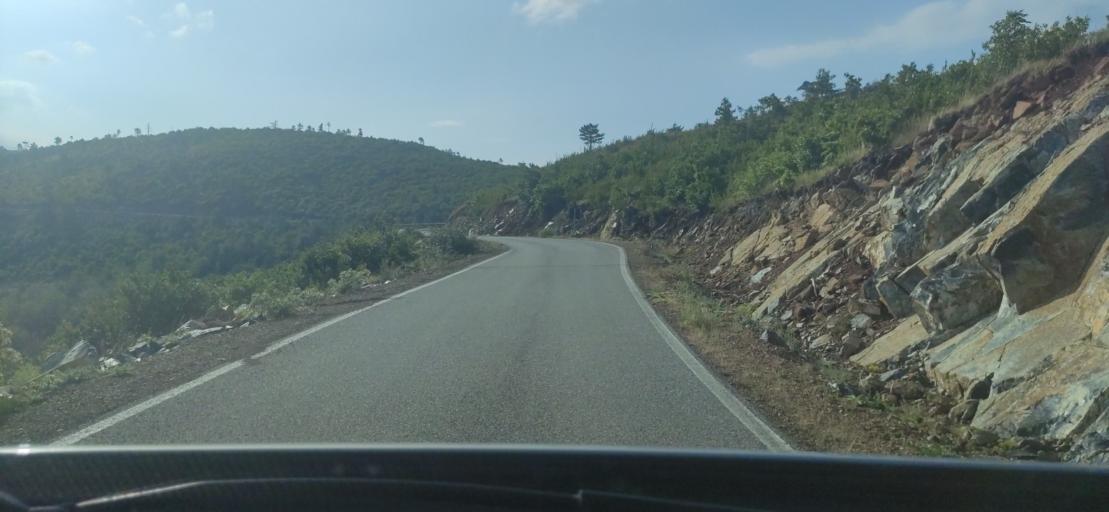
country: AL
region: Shkoder
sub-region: Rrethi i Pukes
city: Iballe
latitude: 42.1717
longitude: 20.0062
